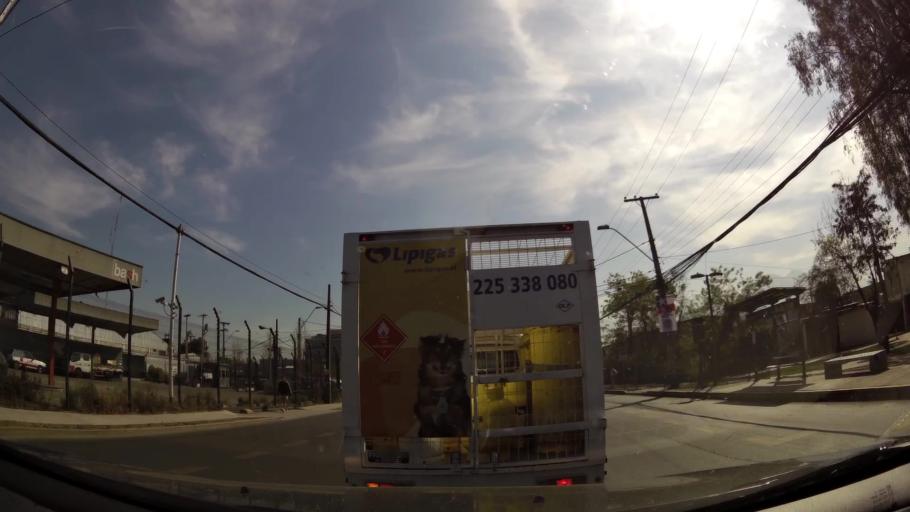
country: CL
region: Santiago Metropolitan
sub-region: Provincia de Santiago
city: Santiago
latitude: -33.4038
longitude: -70.6430
